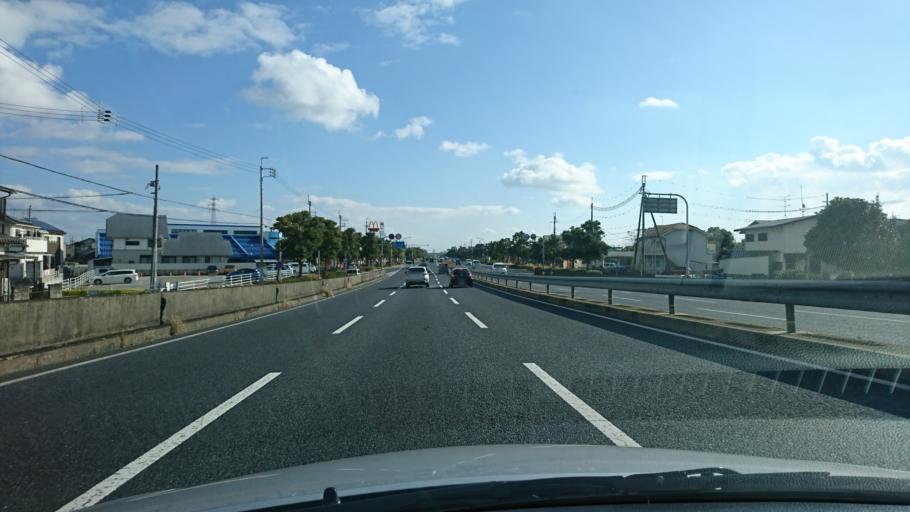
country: JP
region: Hyogo
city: Kakogawacho-honmachi
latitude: 34.7635
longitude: 134.8132
